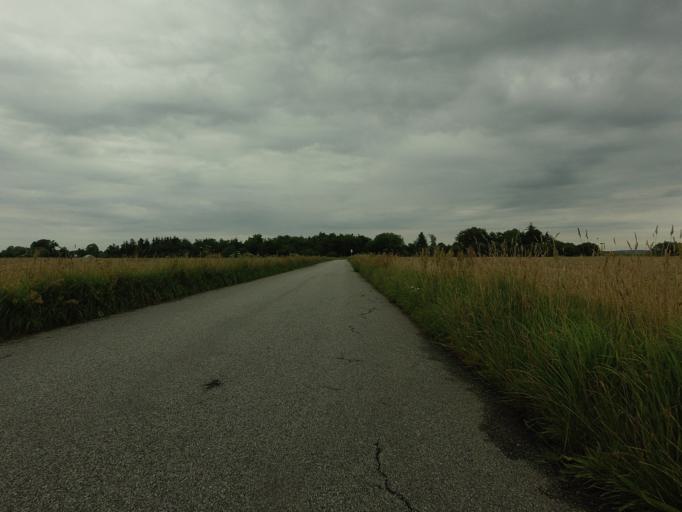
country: DK
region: North Denmark
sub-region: Alborg Kommune
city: Vadum
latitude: 57.1110
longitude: 9.8812
